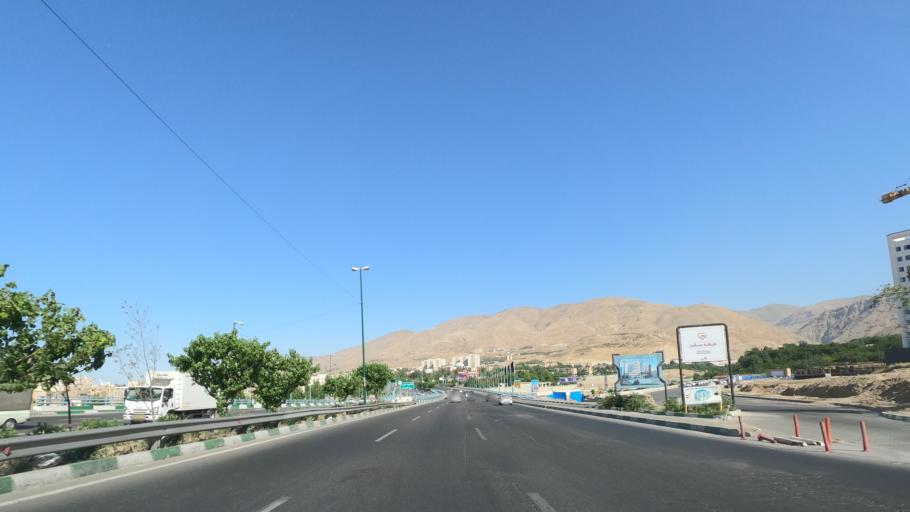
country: IR
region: Tehran
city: Tajrish
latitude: 35.7552
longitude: 51.2703
